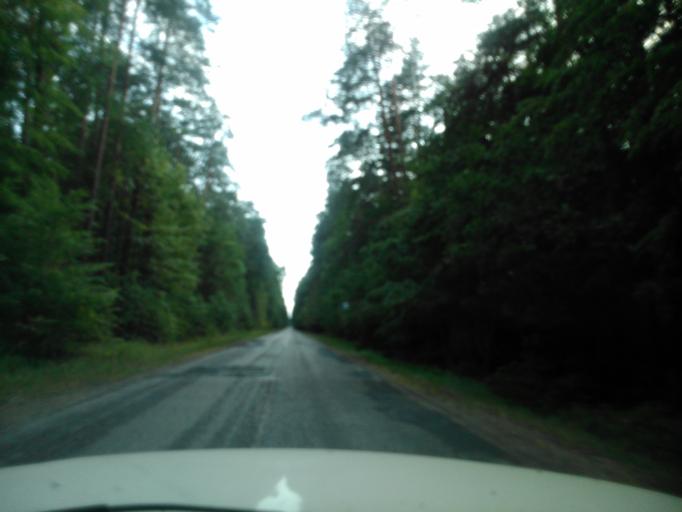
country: PL
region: Kujawsko-Pomorskie
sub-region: Powiat wabrzeski
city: Debowa Laka
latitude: 53.1893
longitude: 19.1523
